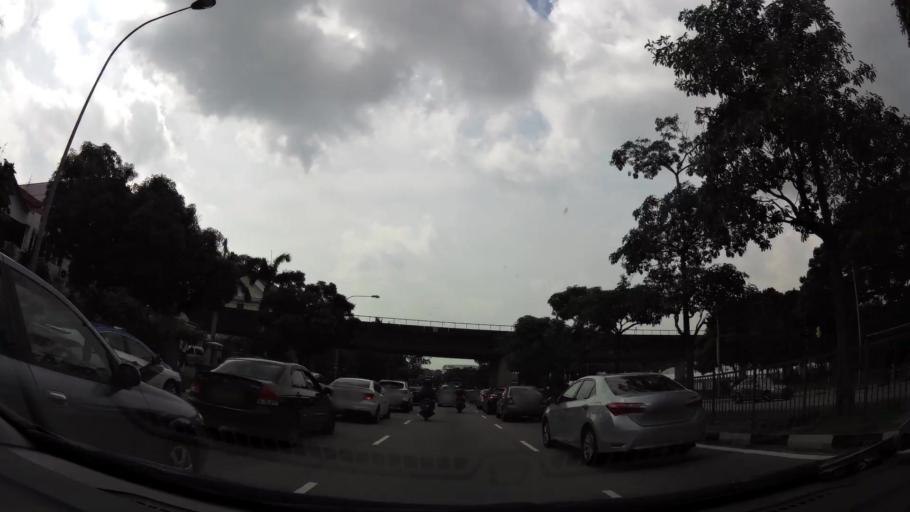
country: SG
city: Singapore
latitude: 1.3205
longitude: 103.9051
